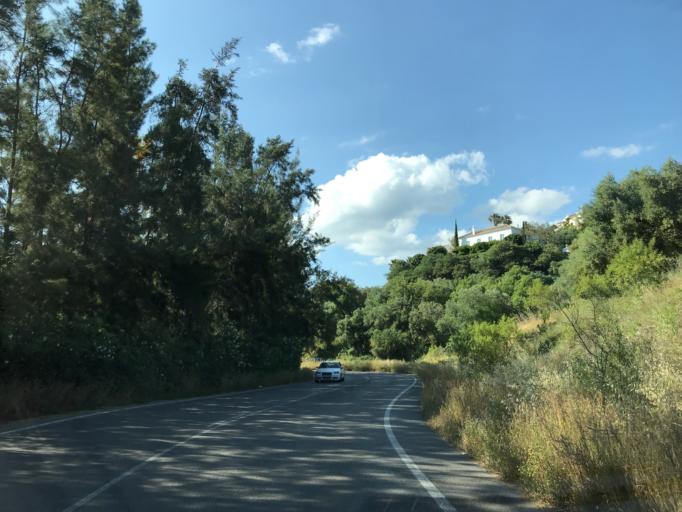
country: ES
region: Andalusia
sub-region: Provincia de Malaga
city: Benahavis
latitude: 36.5060
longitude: -5.0140
